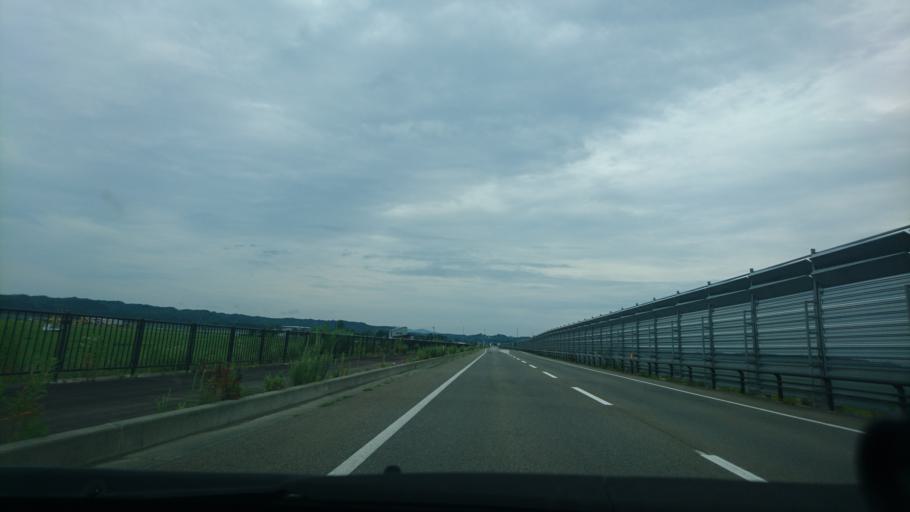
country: JP
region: Akita
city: Omagari
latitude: 39.5057
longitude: 140.3983
